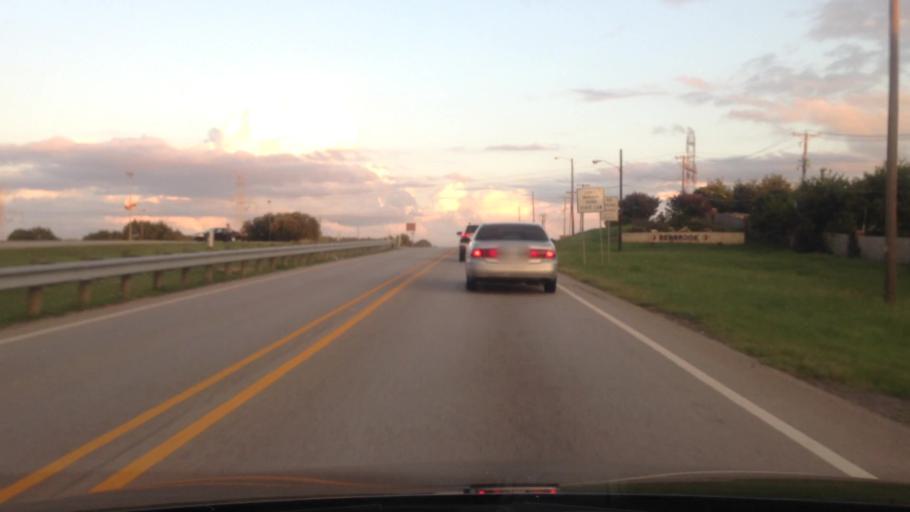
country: US
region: Texas
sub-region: Tarrant County
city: Benbrook
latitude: 32.6729
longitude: -97.4962
